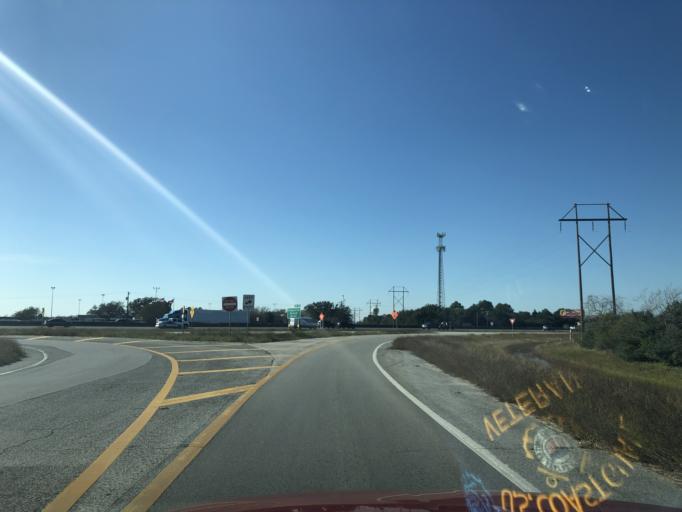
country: US
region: Texas
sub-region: Galveston County
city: Hitchcock
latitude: 29.3926
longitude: -95.0210
